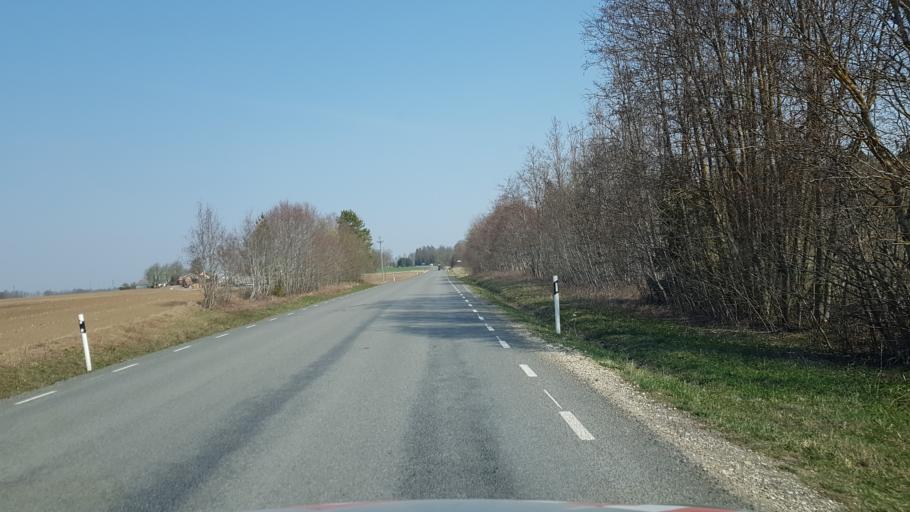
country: EE
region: Raplamaa
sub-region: Kehtna vald
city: Kehtna
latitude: 59.0456
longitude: 24.9451
